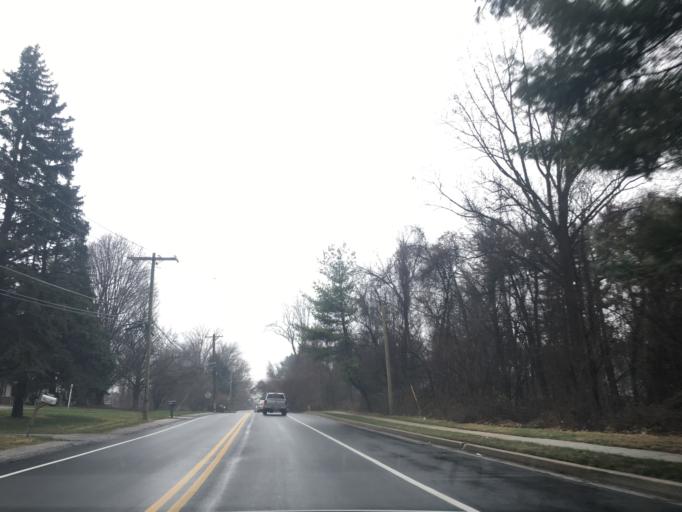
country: US
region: Maryland
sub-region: Baltimore County
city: Garrison
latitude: 39.3948
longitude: -76.7560
